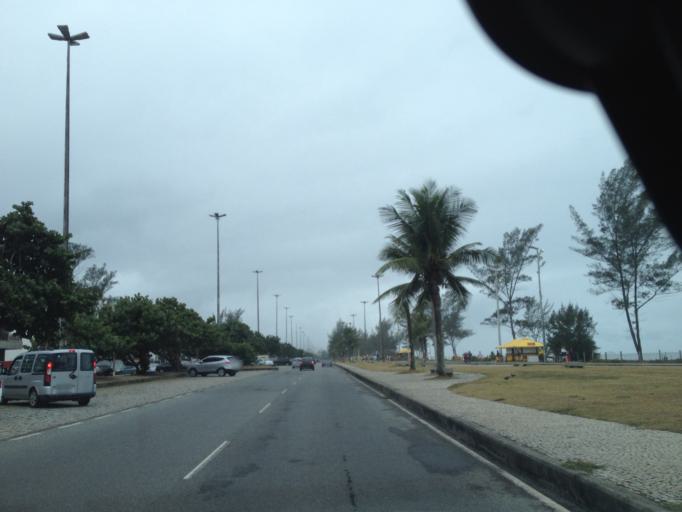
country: BR
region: Rio de Janeiro
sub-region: Nilopolis
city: Nilopolis
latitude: -23.0278
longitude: -43.4652
